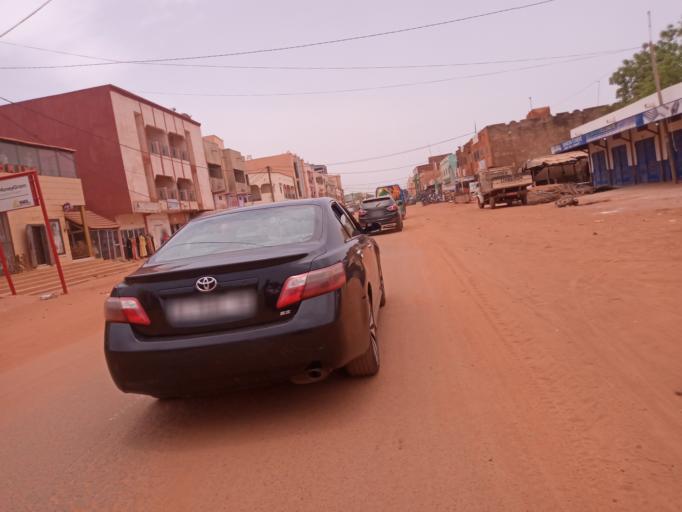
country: ML
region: Bamako
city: Bamako
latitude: 12.5786
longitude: -8.0151
